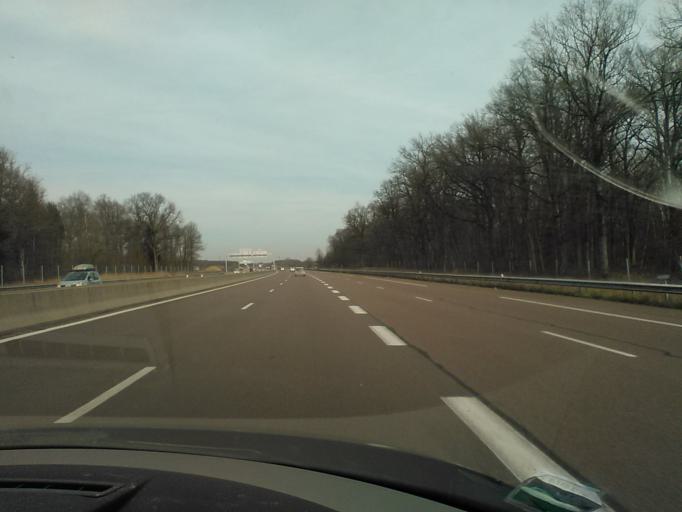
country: FR
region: Bourgogne
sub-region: Departement de la Cote-d'Or
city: Chevigny-Saint-Sauveur
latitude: 47.2794
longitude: 5.1515
